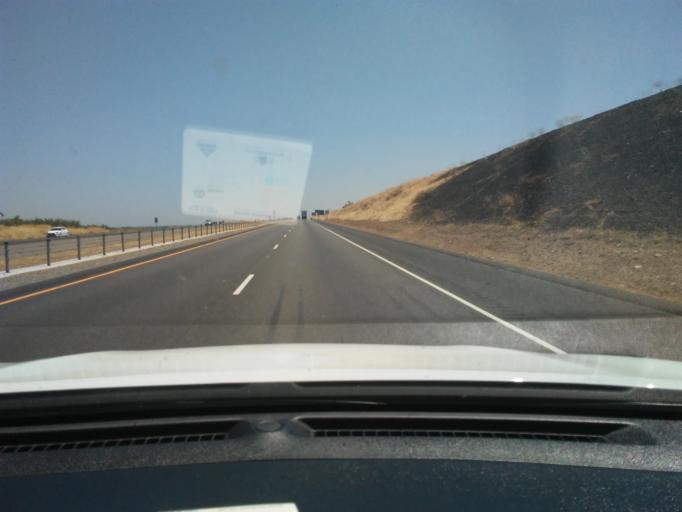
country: US
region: California
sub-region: Stanislaus County
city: Patterson
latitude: 37.5511
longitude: -121.2822
